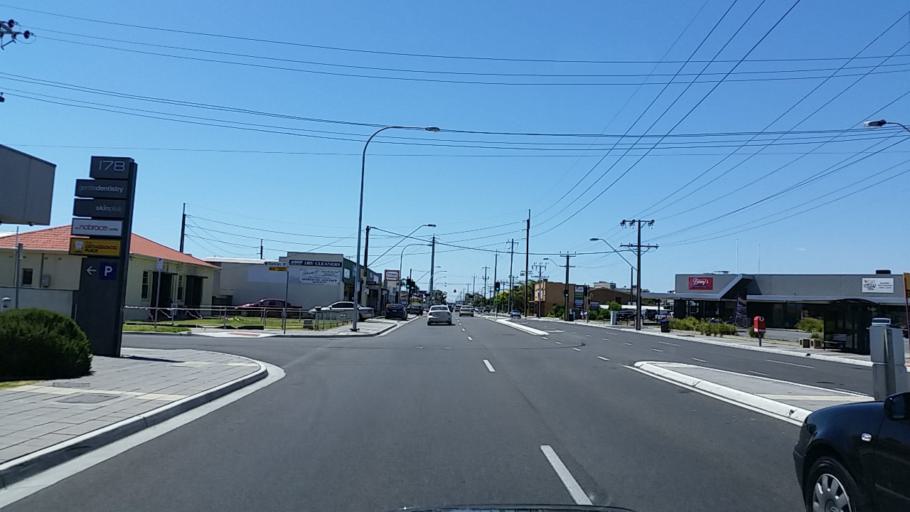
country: AU
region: South Australia
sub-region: Charles Sturt
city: Findon
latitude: -34.8937
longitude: 138.5317
